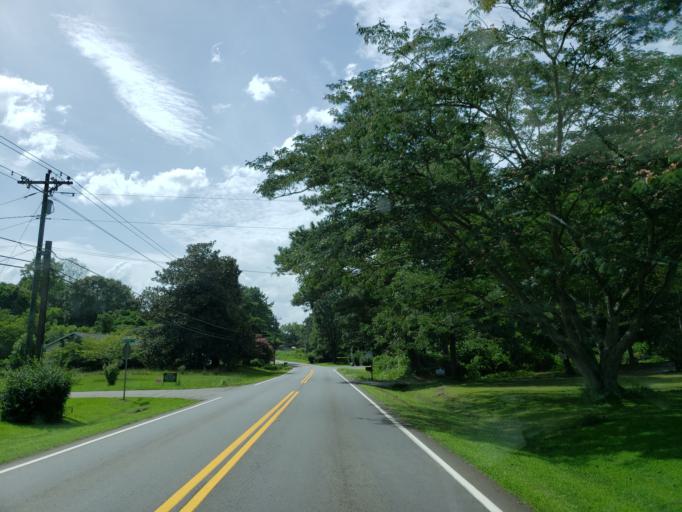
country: US
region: Georgia
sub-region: Cherokee County
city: Canton
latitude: 34.3025
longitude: -84.4521
